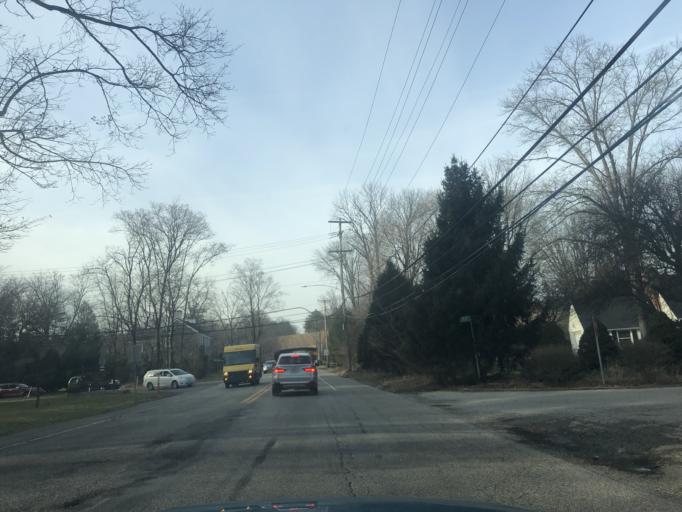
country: US
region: Pennsylvania
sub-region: Montgomery County
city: Fort Washington
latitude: 40.1250
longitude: -75.2215
